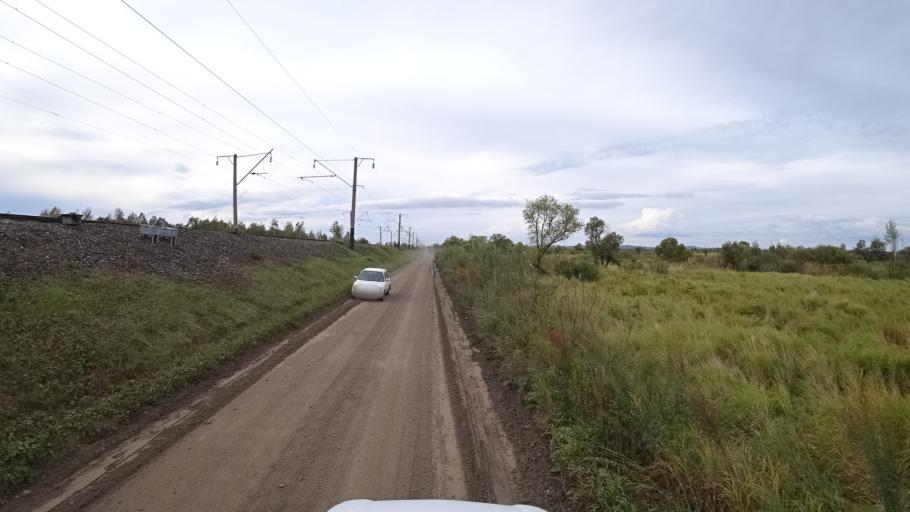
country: RU
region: Amur
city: Arkhara
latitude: 49.3553
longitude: 130.1548
